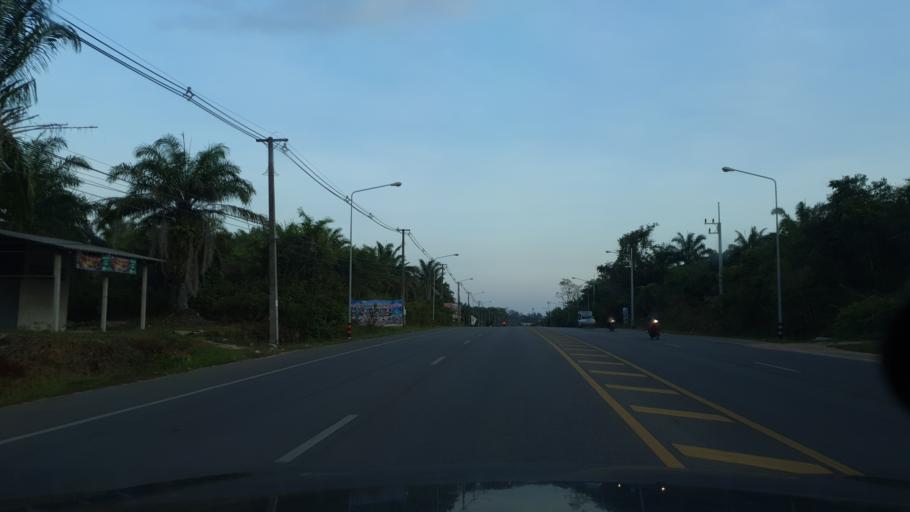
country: TH
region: Phangnga
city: Ban Ao Nang
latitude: 8.0385
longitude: 98.8528
